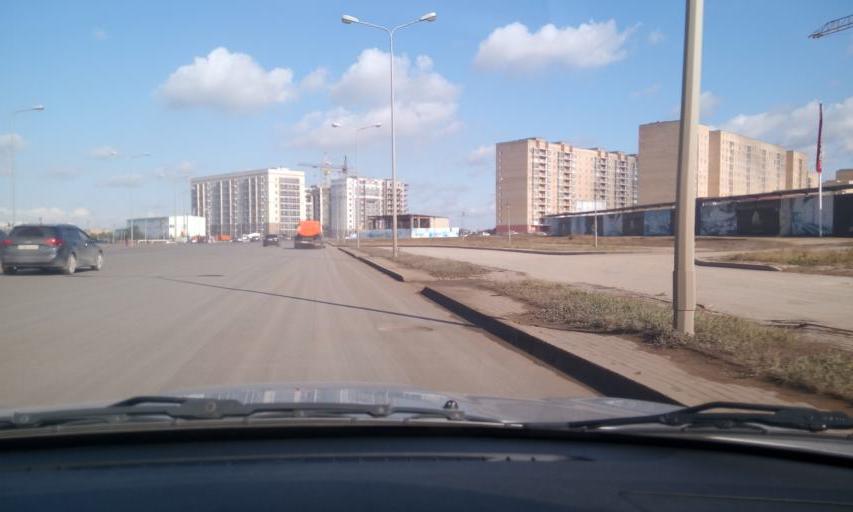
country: KZ
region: Astana Qalasy
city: Astana
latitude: 51.1237
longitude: 71.4868
